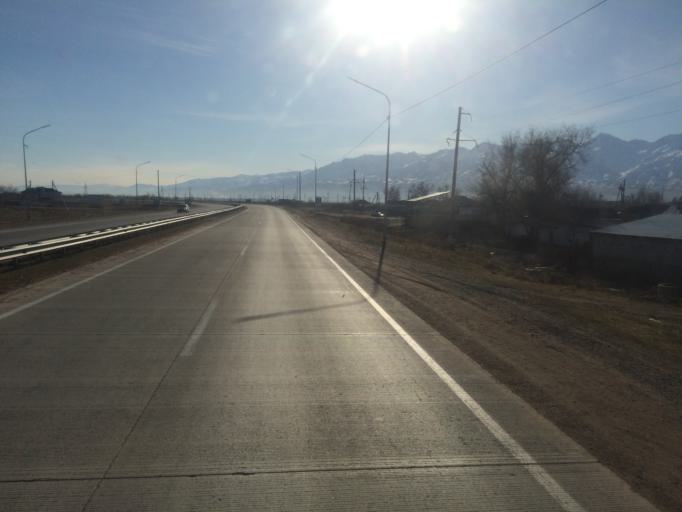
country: KG
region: Talas
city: Ivanovo-Alekseyevka
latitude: 42.9927
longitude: 72.1117
